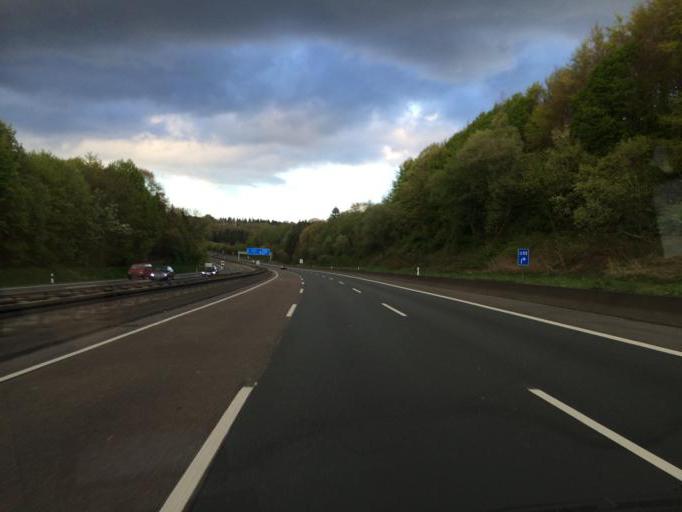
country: DE
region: North Rhine-Westphalia
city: Wermelskirchen
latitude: 51.1262
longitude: 7.1807
